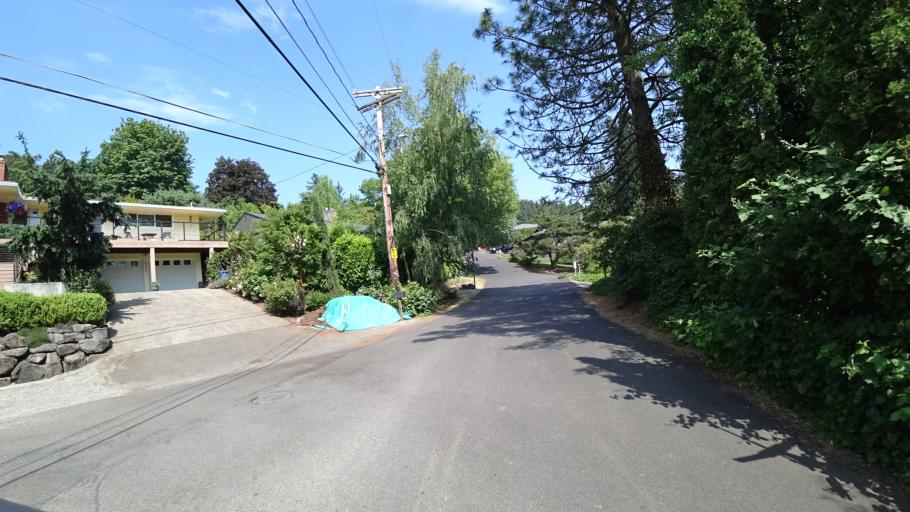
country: US
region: Oregon
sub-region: Multnomah County
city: Portland
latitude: 45.4906
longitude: -122.7057
